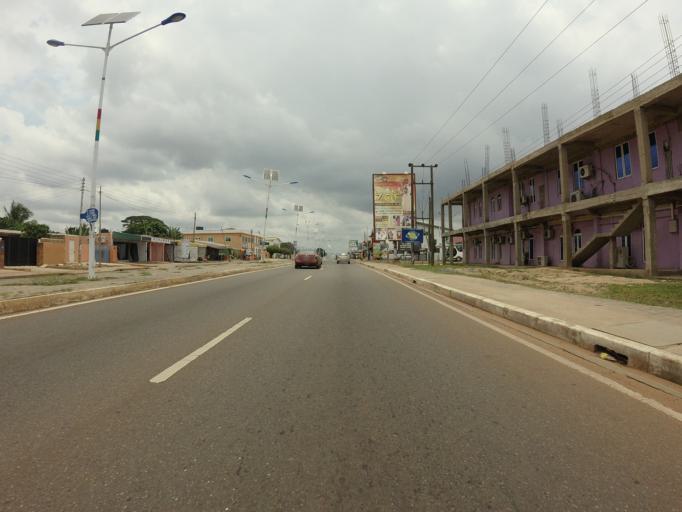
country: GH
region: Greater Accra
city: Medina Estates
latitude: 5.6641
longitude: -0.1515
